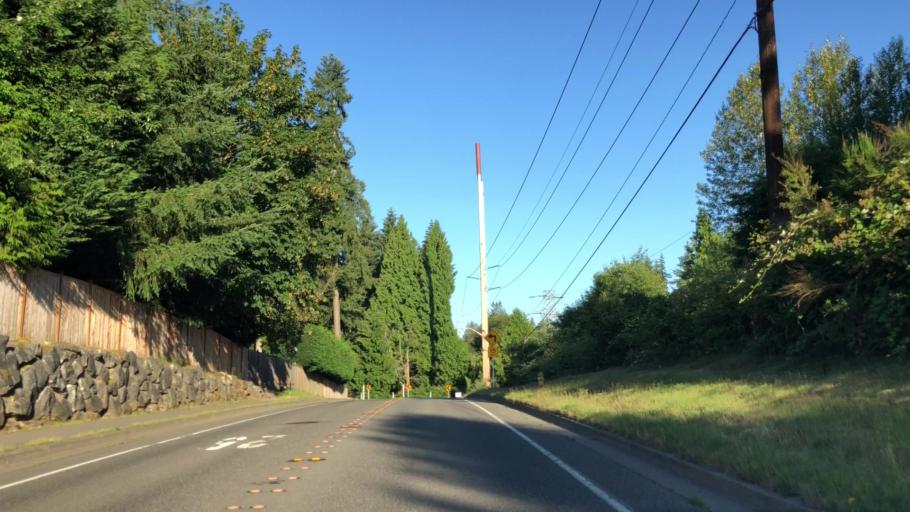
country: US
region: Washington
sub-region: King County
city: Redmond
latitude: 47.6996
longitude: -122.1177
